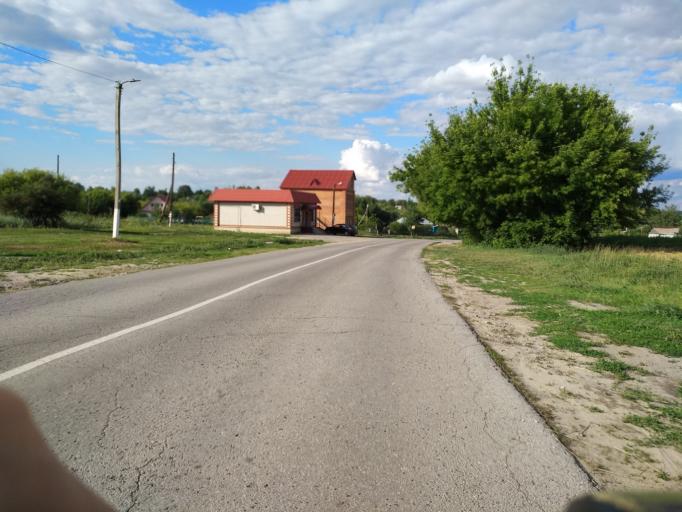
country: RU
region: Lipetsk
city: Dobrinka
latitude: 52.0396
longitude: 40.5540
